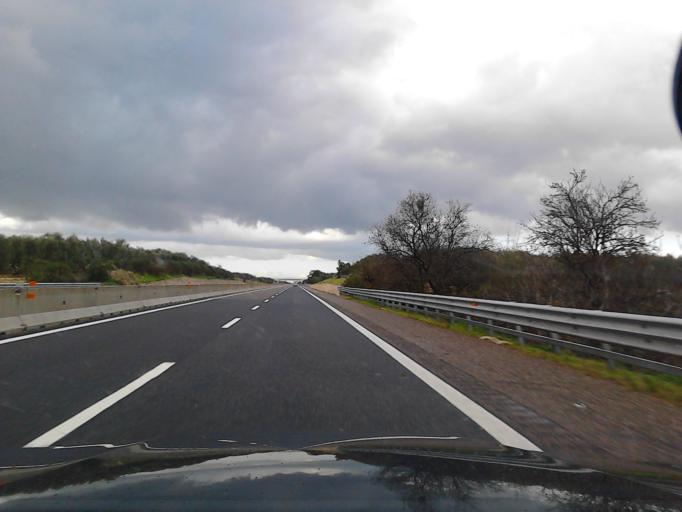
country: IT
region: Apulia
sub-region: Provincia di Bari
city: Molfetta
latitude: 41.1810
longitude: 16.5477
